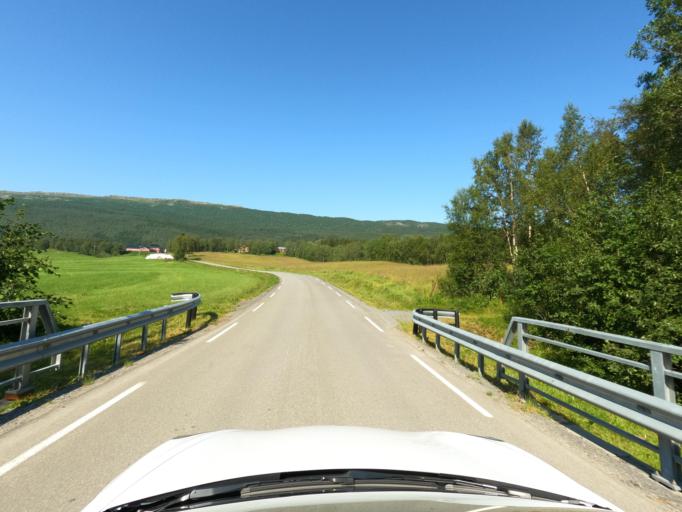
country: NO
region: Nordland
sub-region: Ballangen
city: Ballangen
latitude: 68.3443
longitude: 16.8137
